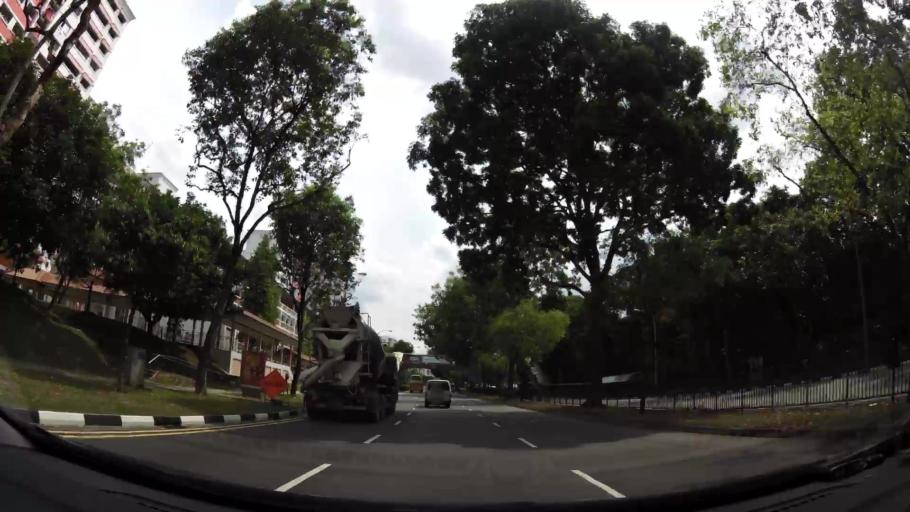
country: MY
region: Johor
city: Johor Bahru
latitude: 1.3890
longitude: 103.7405
